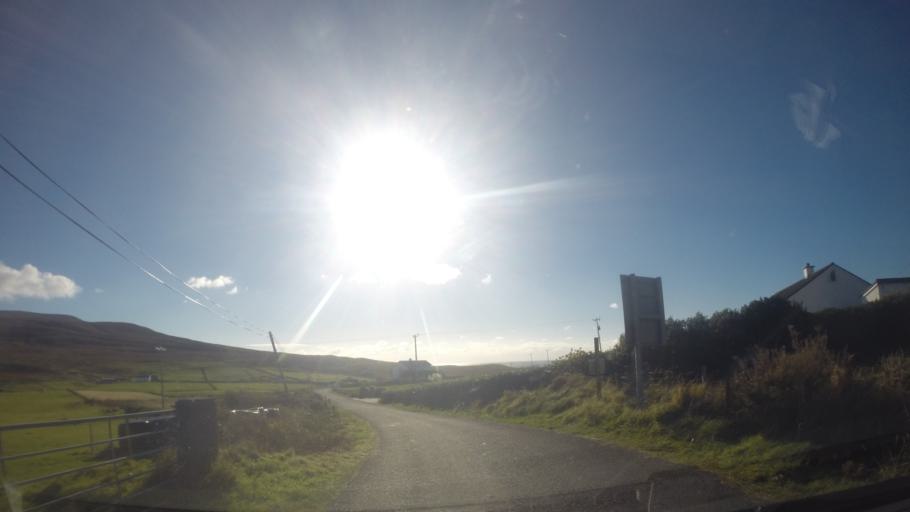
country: IE
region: Ulster
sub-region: County Donegal
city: Killybegs
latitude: 54.6939
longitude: -8.7751
